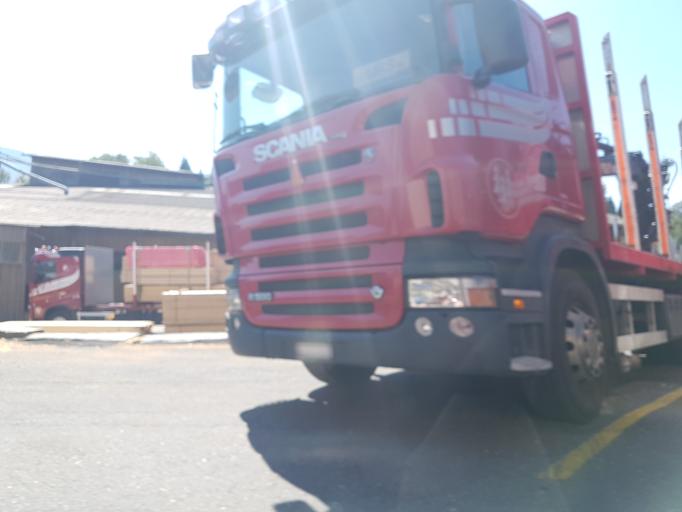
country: CH
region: Lucerne
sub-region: Lucerne-Land District
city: Udligenswil
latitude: 47.0897
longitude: 8.4143
